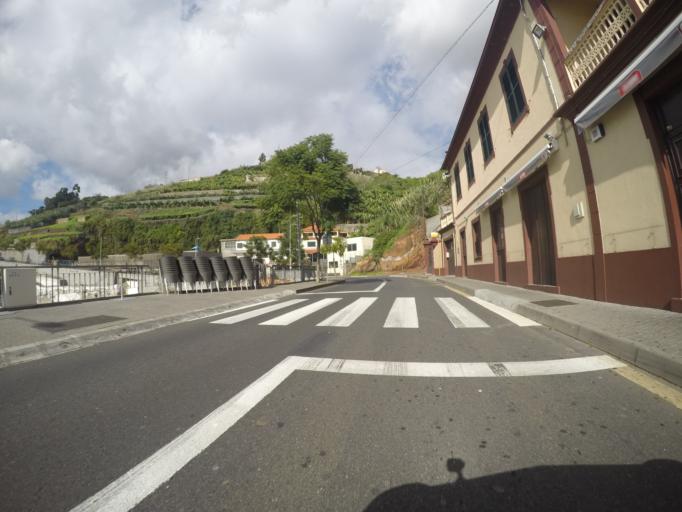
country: PT
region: Madeira
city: Camara de Lobos
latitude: 32.6448
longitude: -16.9553
